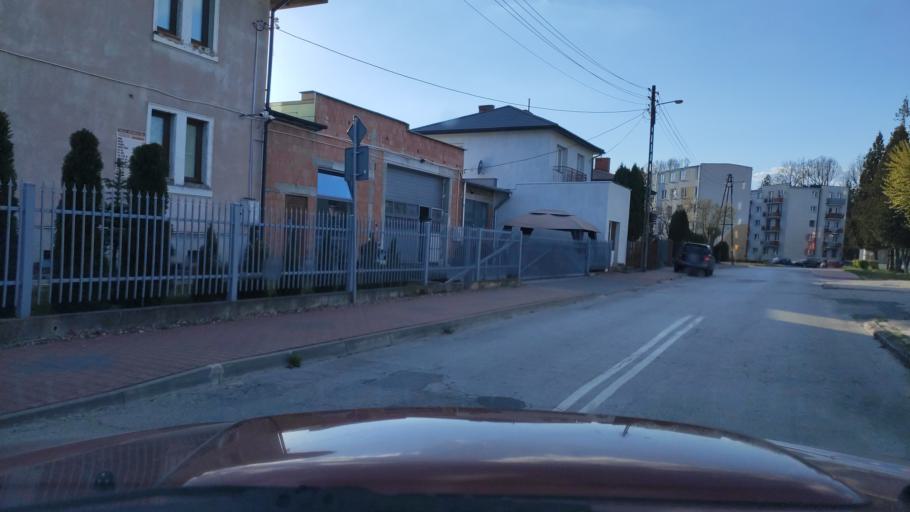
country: PL
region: Masovian Voivodeship
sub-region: Powiat radomski
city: Pionki
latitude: 51.4721
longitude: 21.4401
